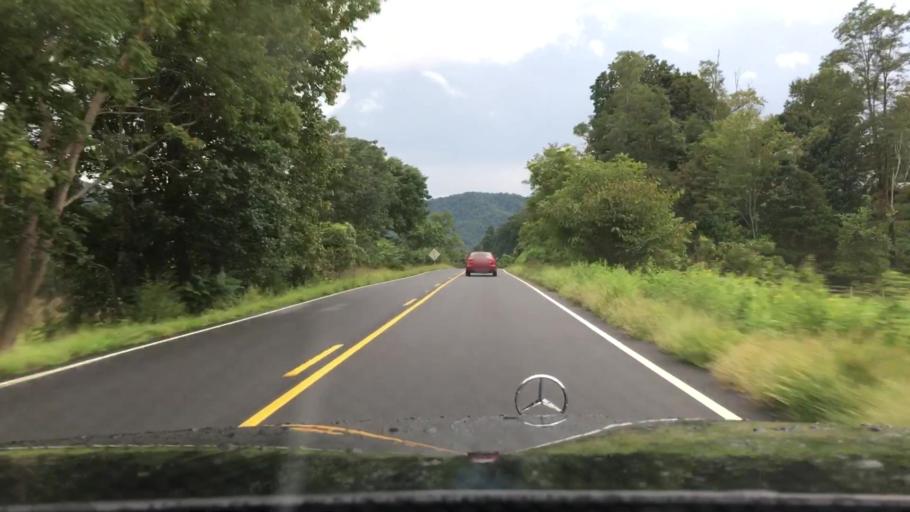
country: US
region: Virginia
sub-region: Nelson County
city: Nellysford
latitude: 37.8778
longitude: -78.9095
